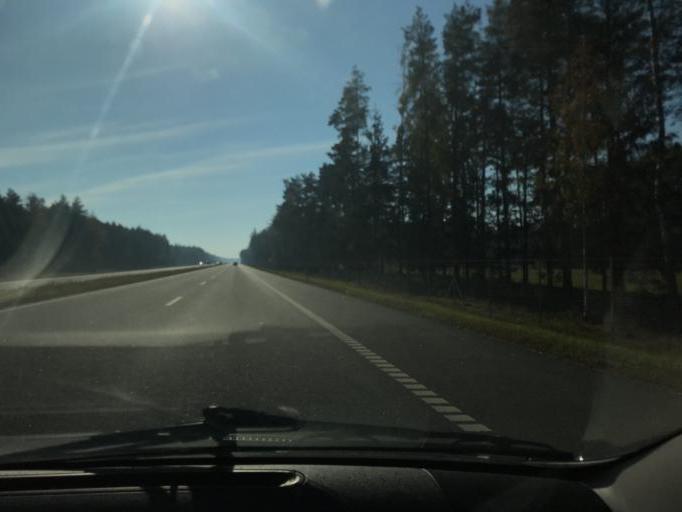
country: BY
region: Minsk
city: Slutsk
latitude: 53.3114
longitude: 27.5386
